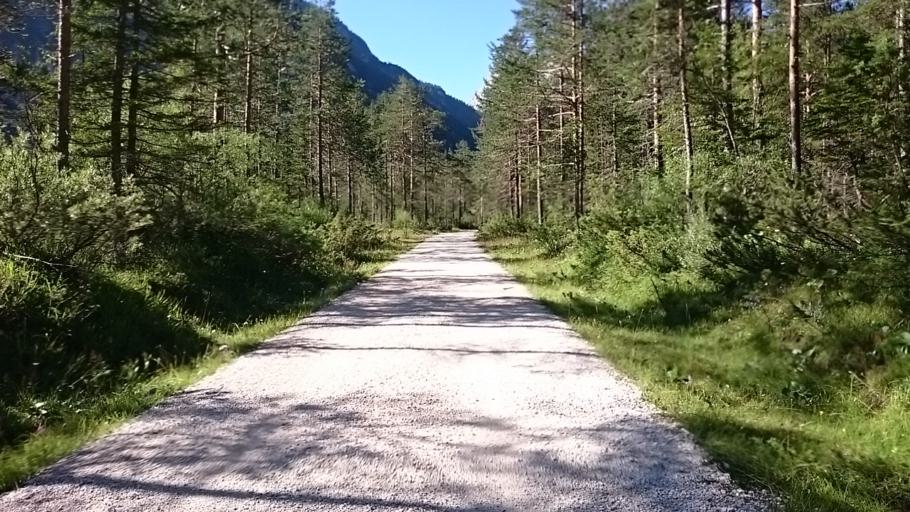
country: IT
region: Trentino-Alto Adige
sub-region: Bolzano
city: Dobbiaco
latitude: 46.6361
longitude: 12.2320
